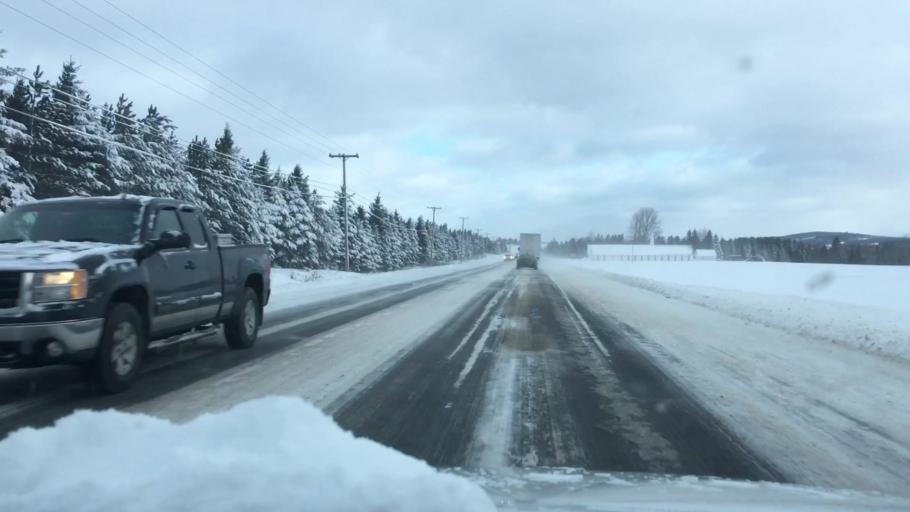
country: US
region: Maine
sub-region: Aroostook County
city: Presque Isle
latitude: 46.7333
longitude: -68.0006
